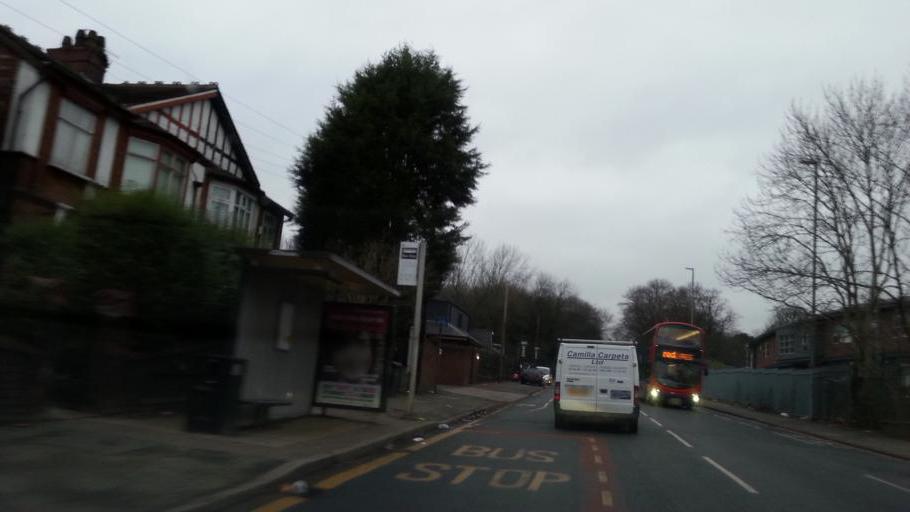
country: GB
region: England
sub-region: Manchester
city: Crumpsall
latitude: 53.5081
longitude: -2.2619
